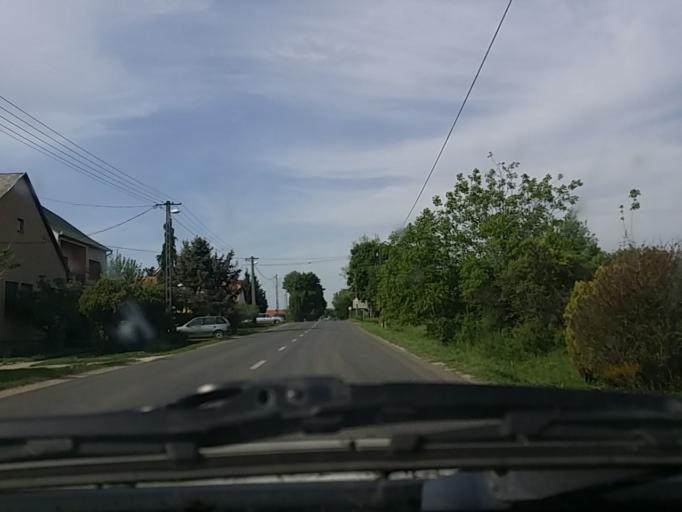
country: HU
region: Baranya
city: Harkany
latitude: 45.9102
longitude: 18.2300
